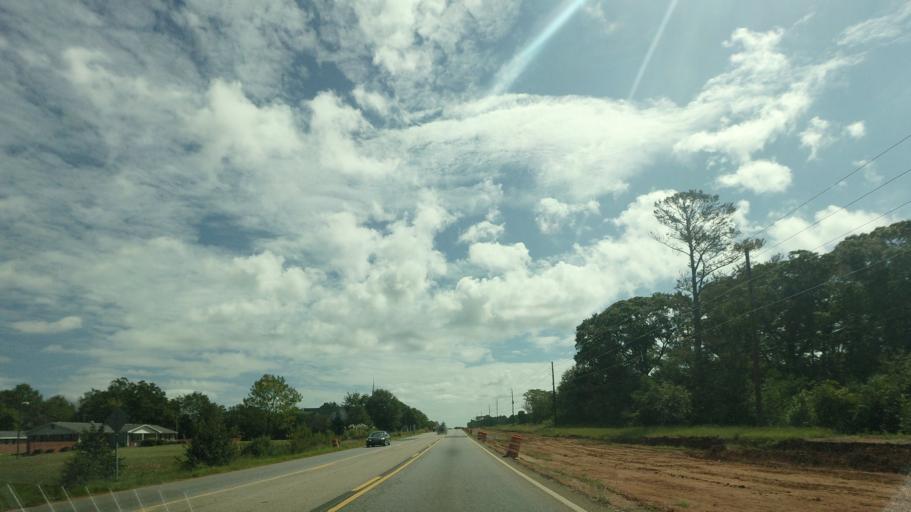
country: US
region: Georgia
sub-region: Houston County
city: Warner Robins
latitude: 32.5545
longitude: -83.6397
